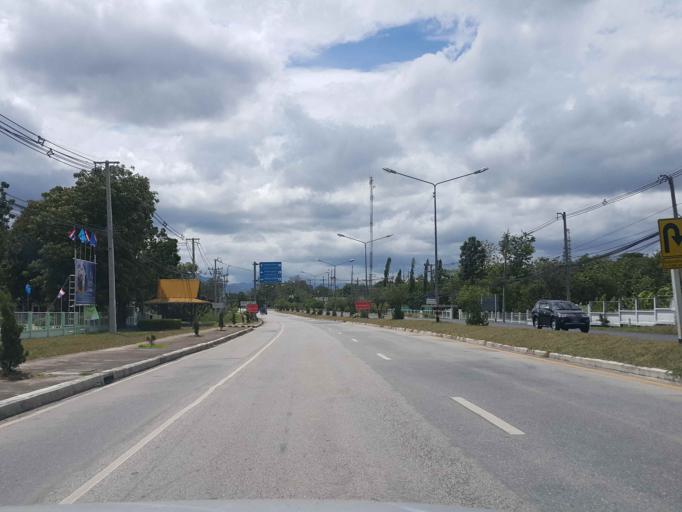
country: TH
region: Tak
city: Tak
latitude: 16.8827
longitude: 99.1350
